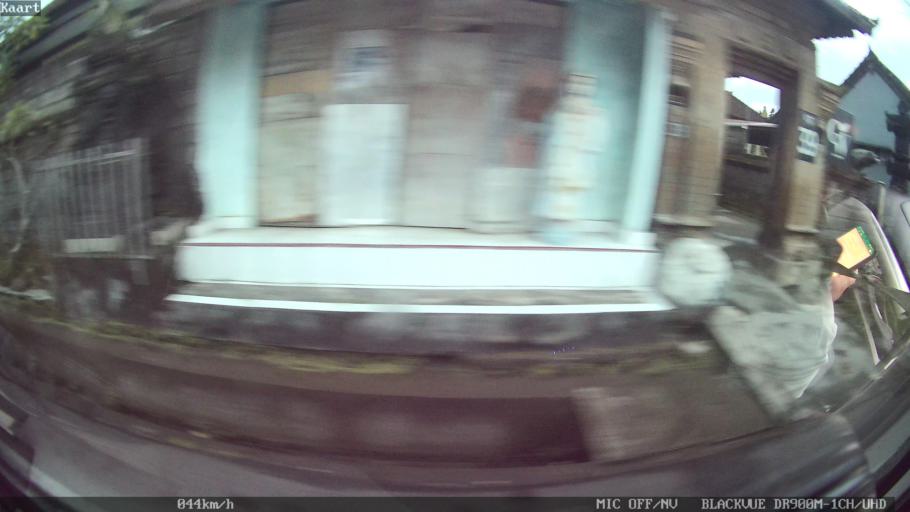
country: ID
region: Bali
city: Banjar Sayanbaleran
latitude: -8.5245
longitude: 115.1861
